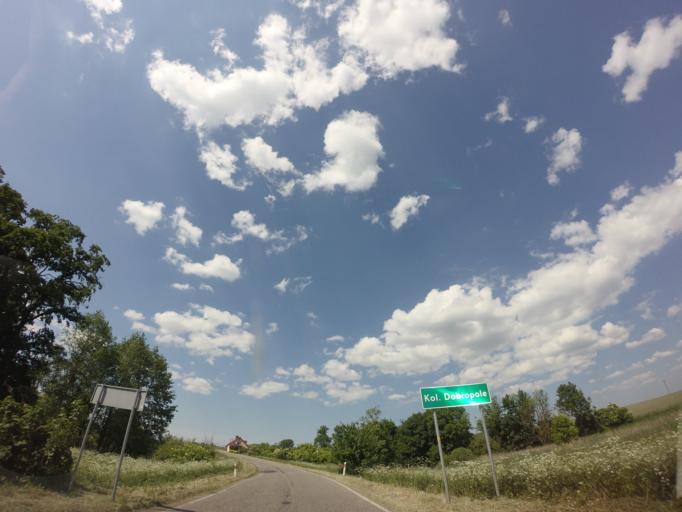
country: PL
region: West Pomeranian Voivodeship
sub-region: Powiat stargardzki
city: Dolice
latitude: 53.1558
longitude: 15.2402
